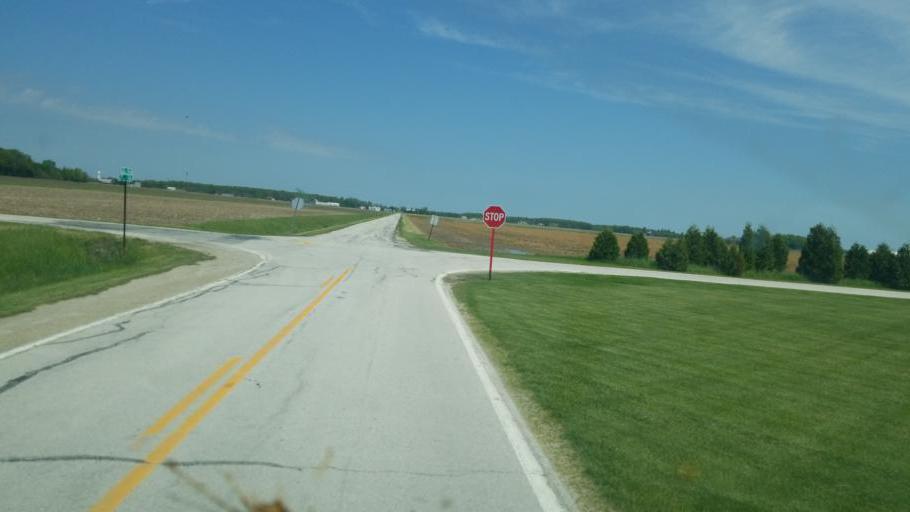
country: US
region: Ohio
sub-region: Ottawa County
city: Oak Harbor
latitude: 41.4581
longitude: -83.2017
